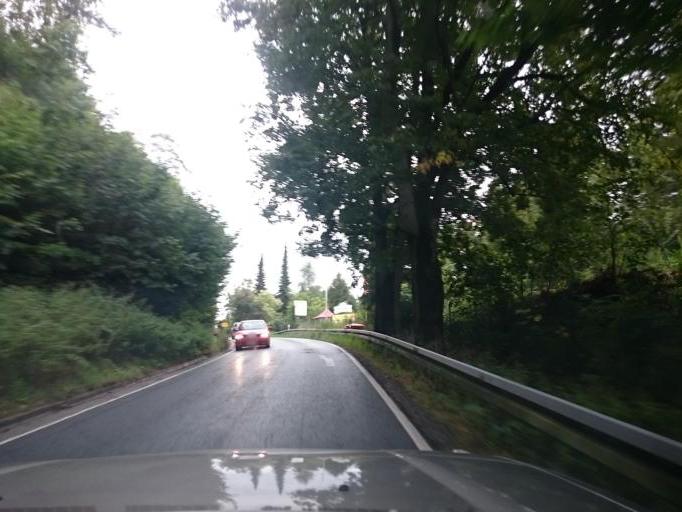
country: DE
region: Bavaria
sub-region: Upper Franconia
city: Gossweinstein
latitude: 49.7754
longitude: 11.3404
